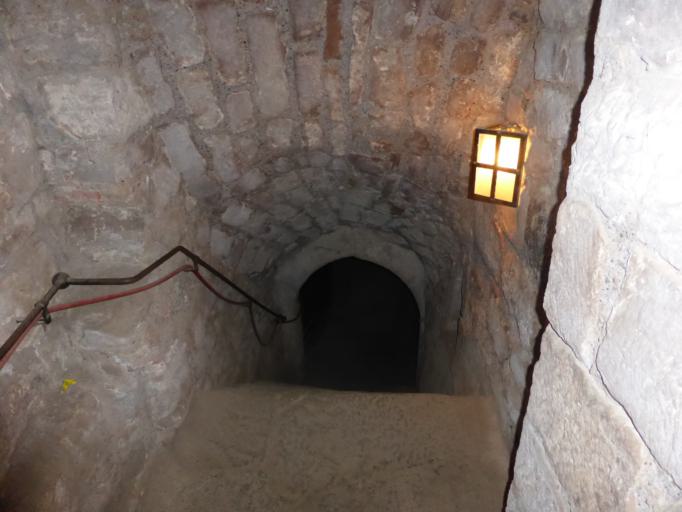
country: DE
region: Thuringia
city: Bornhagen
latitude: 51.3388
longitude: 9.9399
